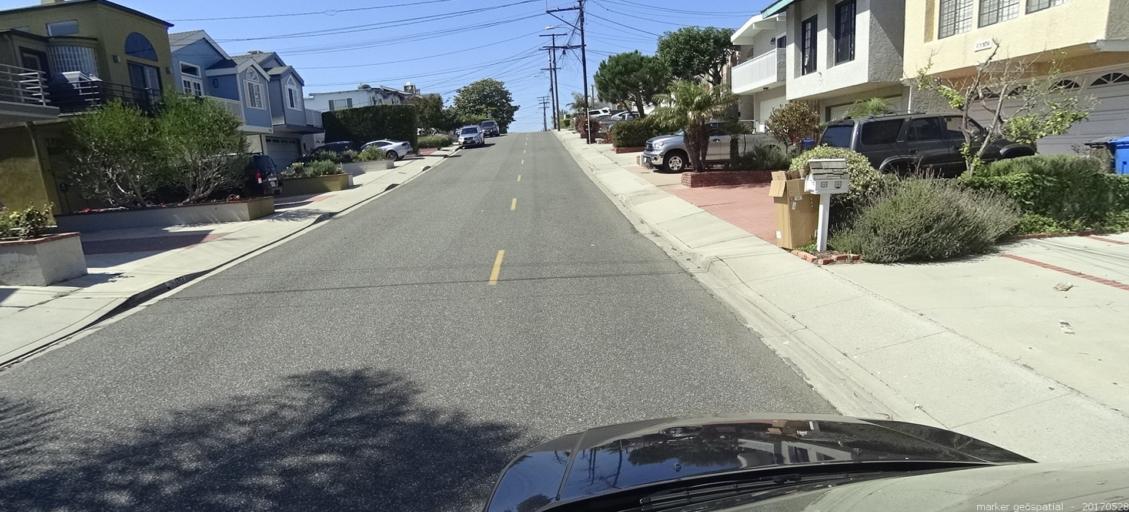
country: US
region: California
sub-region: Los Angeles County
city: Hermosa Beach
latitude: 33.8712
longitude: -118.3851
